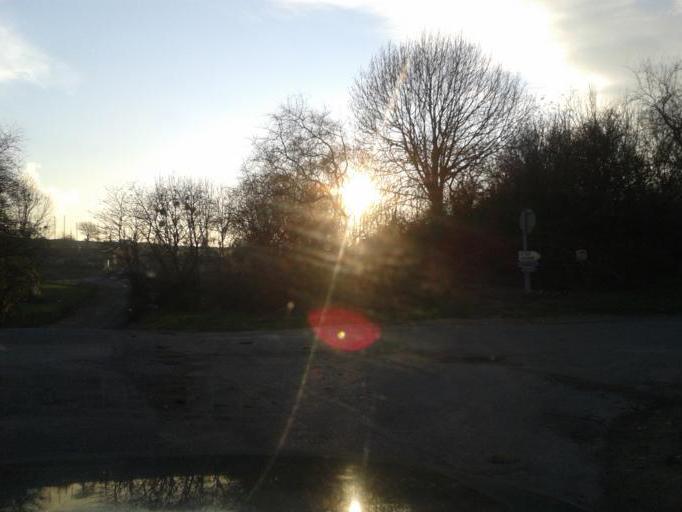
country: FR
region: Centre
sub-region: Departement du Loiret
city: Tavers
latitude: 47.7643
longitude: 1.6025
